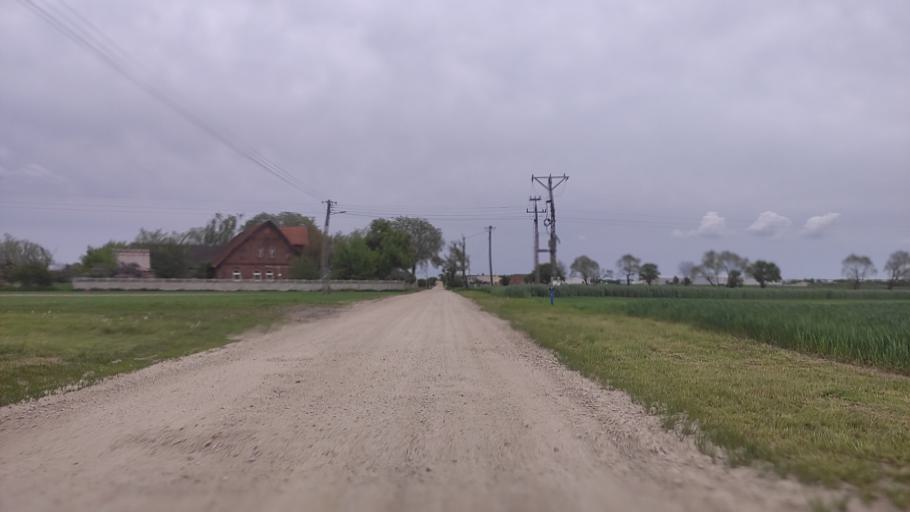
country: PL
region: Greater Poland Voivodeship
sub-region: Powiat poznanski
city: Swarzedz
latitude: 52.4091
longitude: 17.1329
